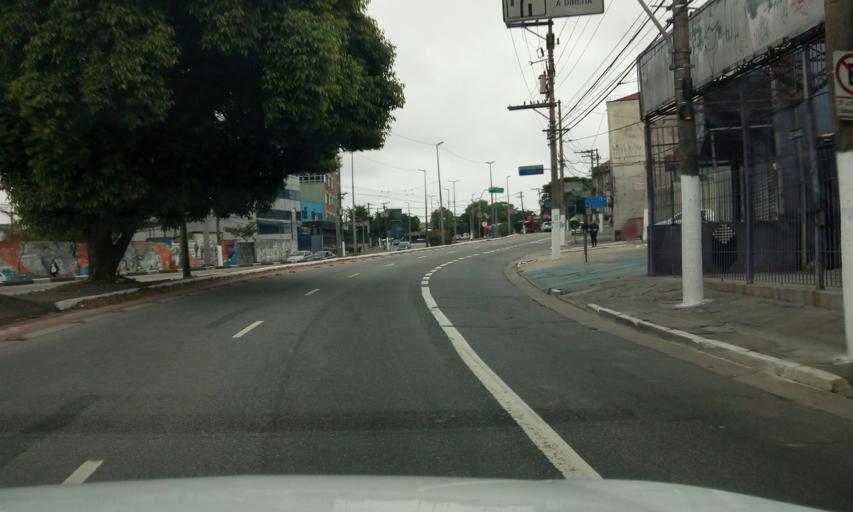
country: BR
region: Sao Paulo
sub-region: Diadema
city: Diadema
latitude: -23.6492
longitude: -46.6404
